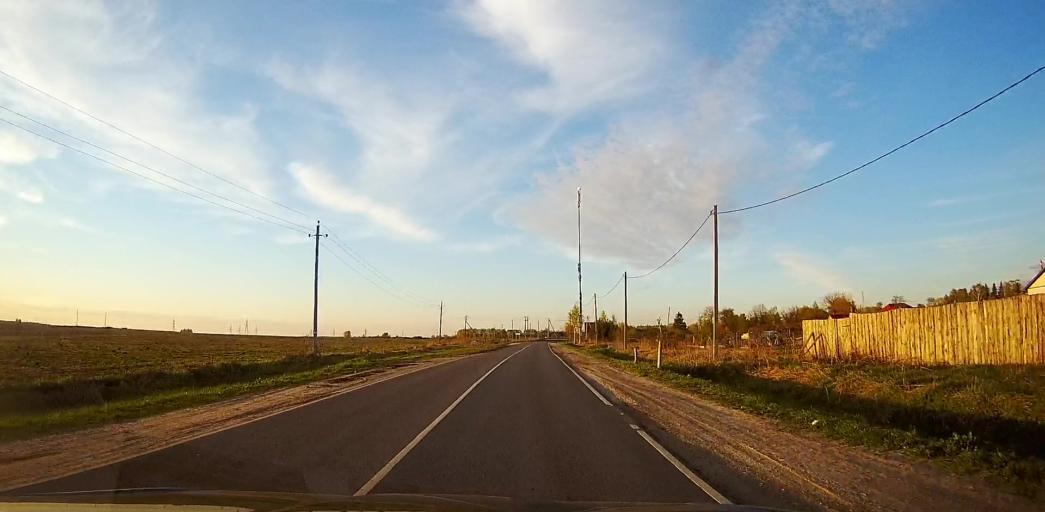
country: RU
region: Moskovskaya
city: Peski
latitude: 55.2139
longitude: 38.6664
